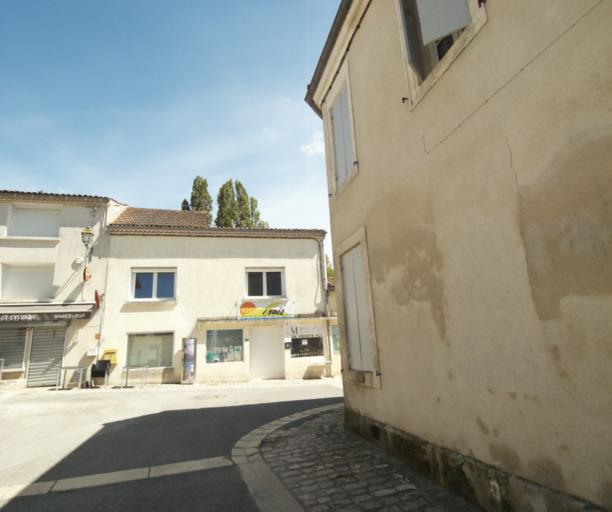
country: FR
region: Poitou-Charentes
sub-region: Departement de la Charente-Maritime
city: Chaniers
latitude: 45.7388
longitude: -0.5055
